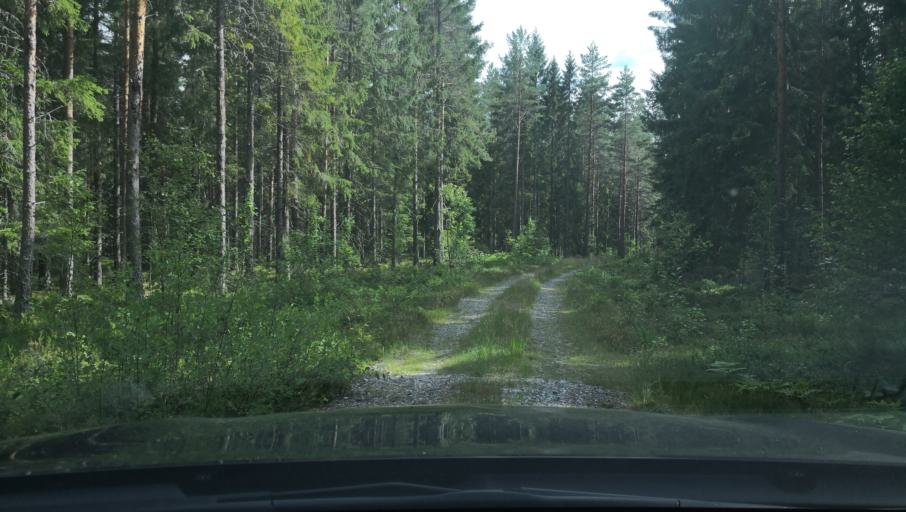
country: SE
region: Vaestmanland
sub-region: Surahammars Kommun
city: Surahammar
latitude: 59.6530
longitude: 16.0977
